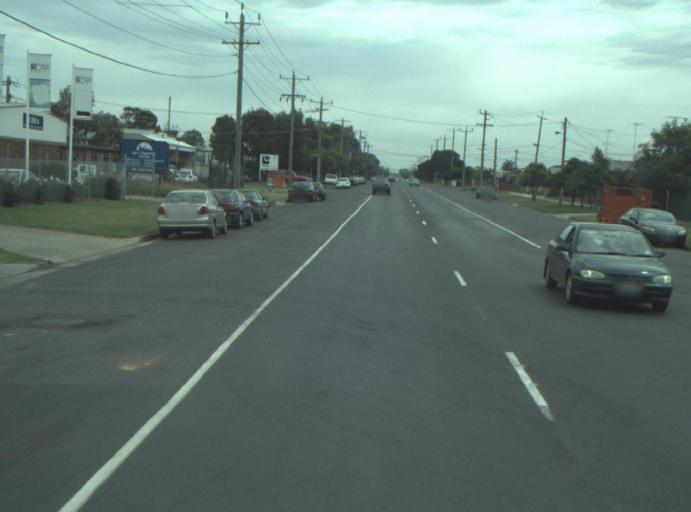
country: AU
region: Victoria
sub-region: Greater Geelong
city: Breakwater
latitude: -38.1850
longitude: 144.3814
